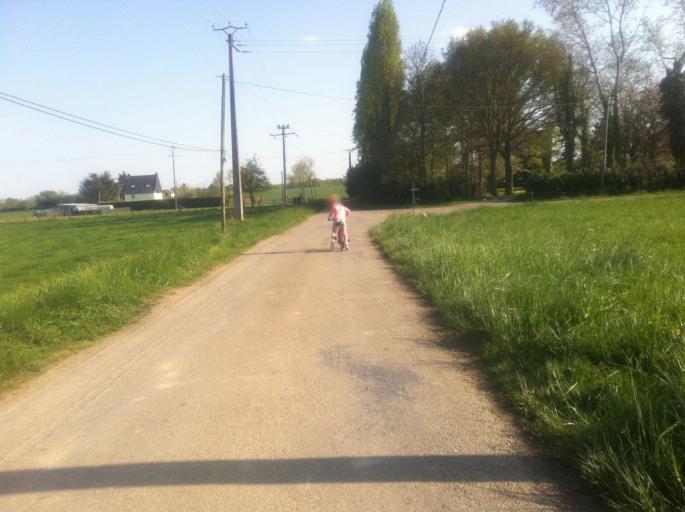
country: FR
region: Brittany
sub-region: Departement d'Ille-et-Vilaine
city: Bruz
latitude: 48.0145
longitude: -1.7274
